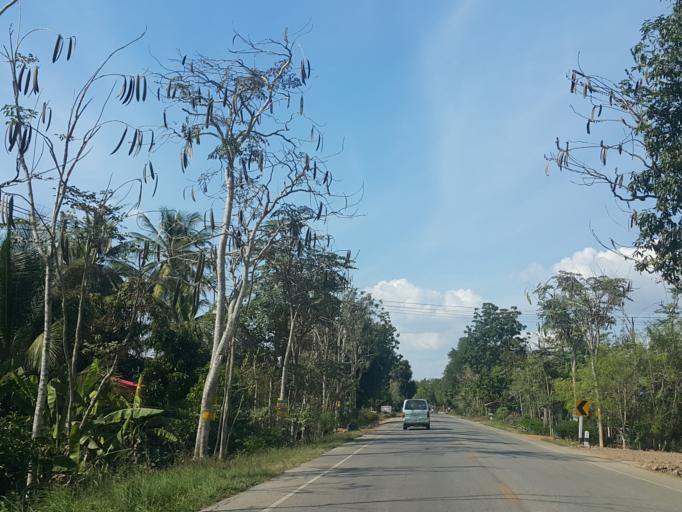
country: TH
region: Sukhothai
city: Sawankhalok
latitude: 17.2649
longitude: 99.8350
